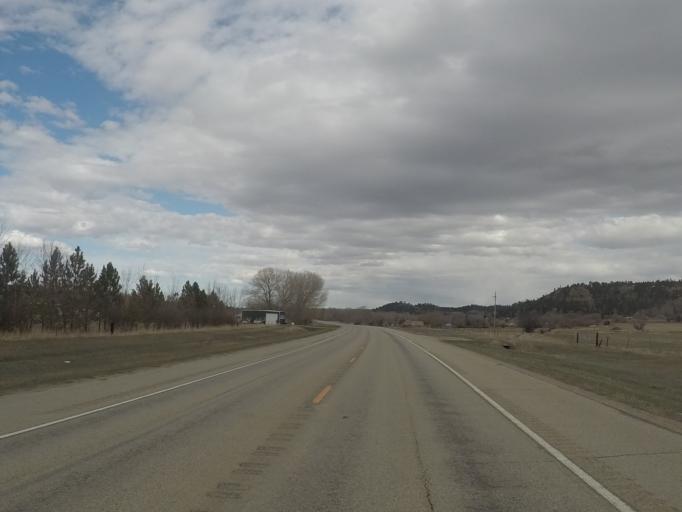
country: US
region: Montana
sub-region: Stillwater County
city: Columbus
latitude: 45.4725
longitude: -109.0062
